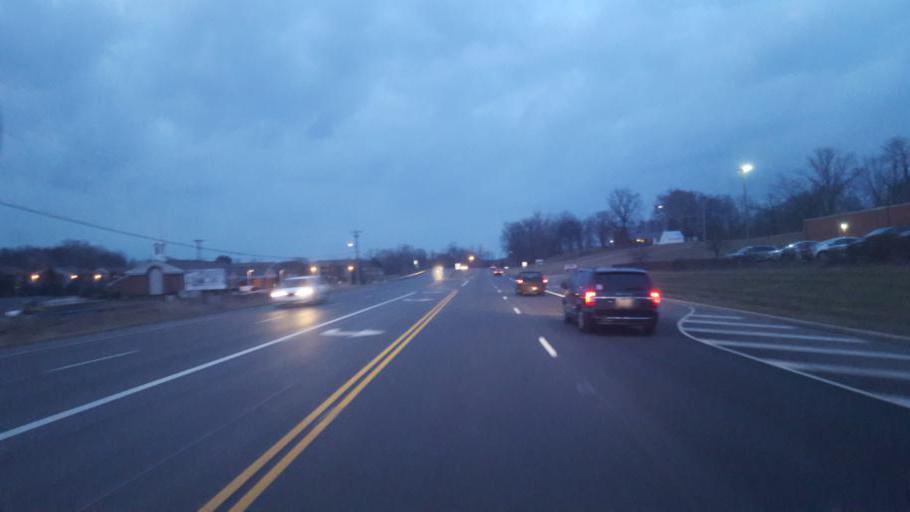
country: US
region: Ohio
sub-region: Ross County
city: Chillicothe
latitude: 39.3738
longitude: -82.9756
